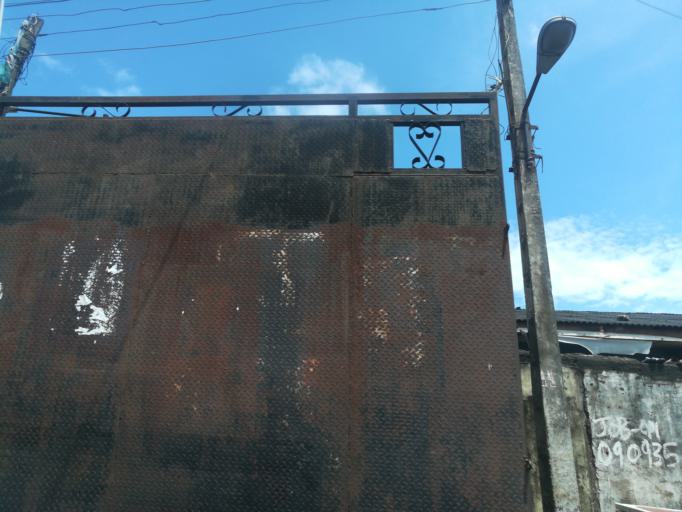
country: NG
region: Lagos
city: Agege
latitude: 6.6180
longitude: 3.3323
